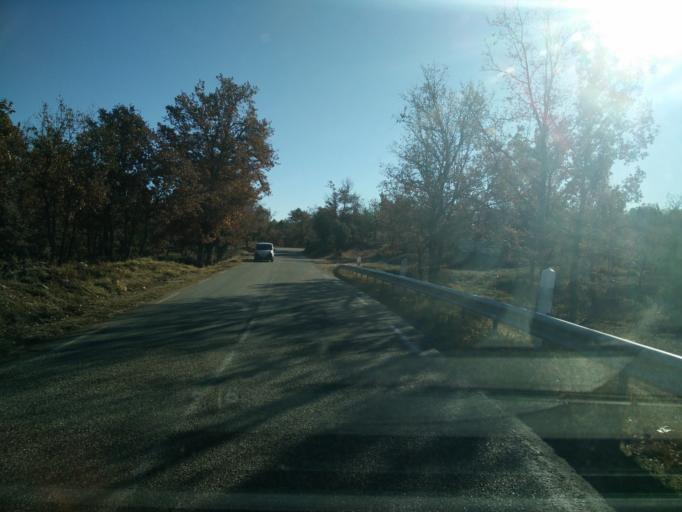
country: FR
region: Provence-Alpes-Cote d'Azur
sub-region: Departement du Var
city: Aups
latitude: 43.6018
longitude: 6.2192
